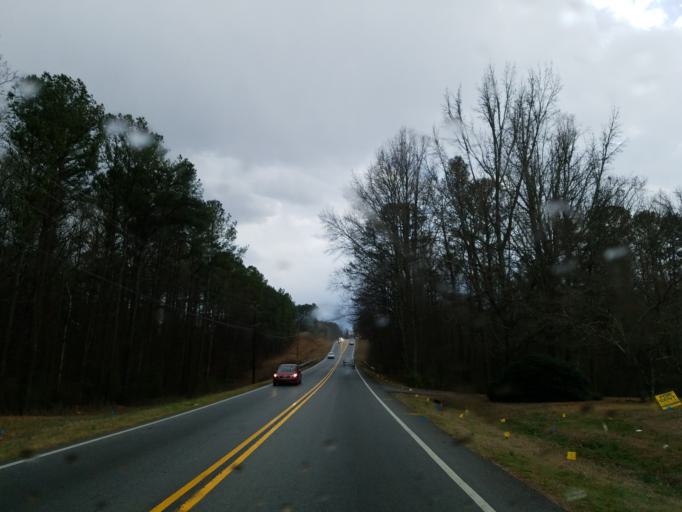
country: US
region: Georgia
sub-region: Henry County
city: Stockbridge
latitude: 33.5702
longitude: -84.2623
